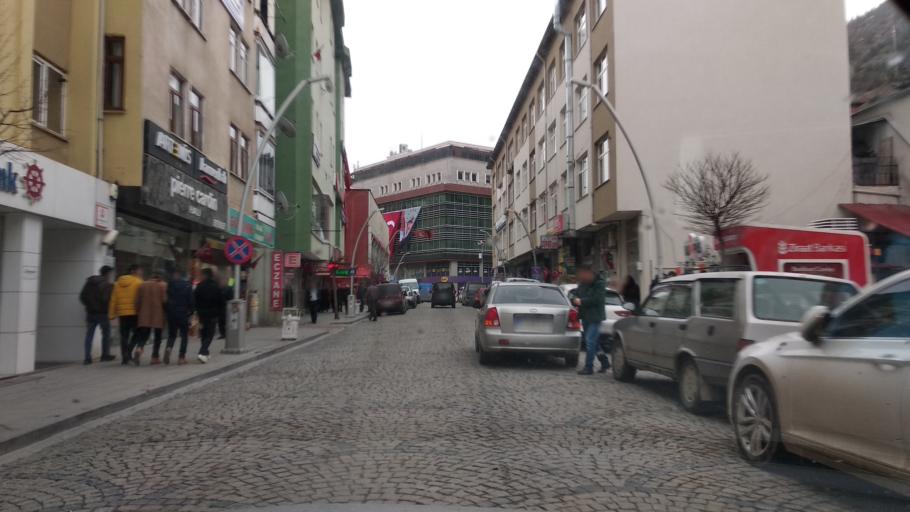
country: TR
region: Gumushane
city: Gumushkhane
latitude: 40.4594
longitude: 39.4775
